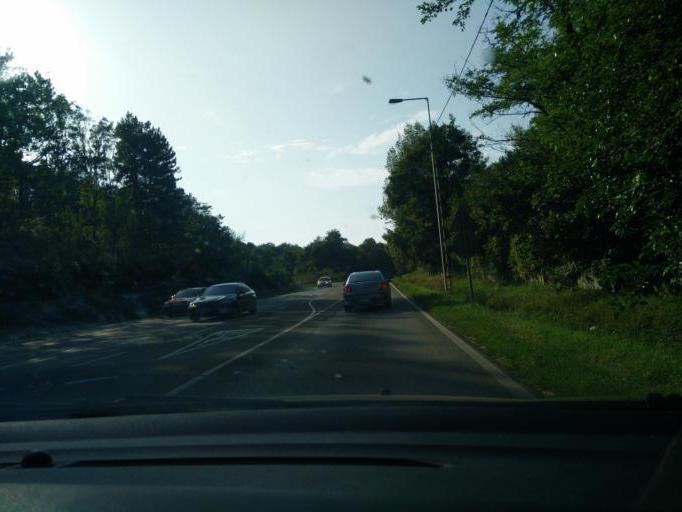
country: HU
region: Pest
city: Piliscsaba
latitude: 47.6289
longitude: 18.8504
